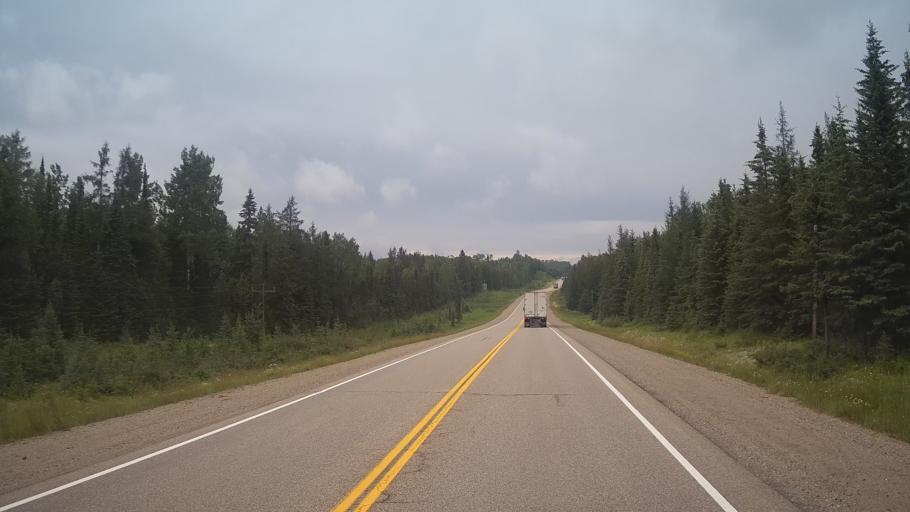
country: CA
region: Ontario
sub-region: Thunder Bay District
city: Thunder Bay
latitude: 48.7448
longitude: -89.8809
